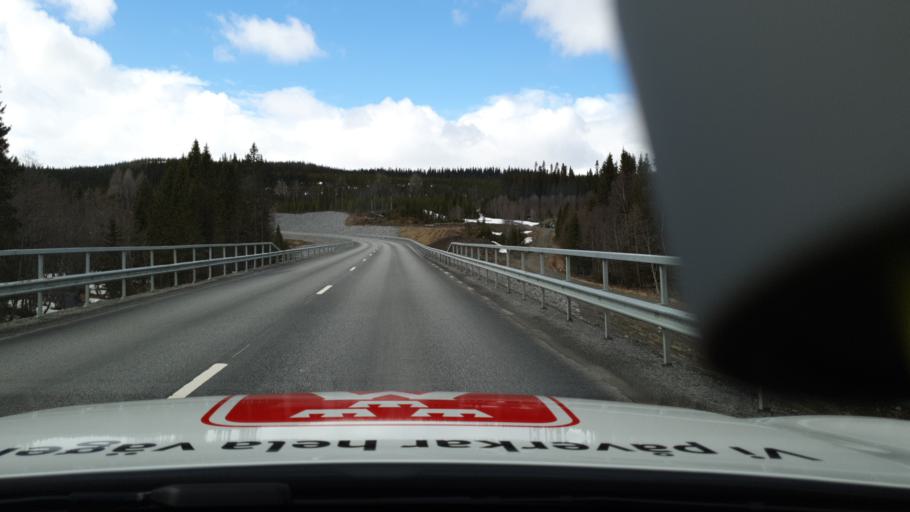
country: SE
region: Jaemtland
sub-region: Are Kommun
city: Are
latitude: 63.3967
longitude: 12.7906
